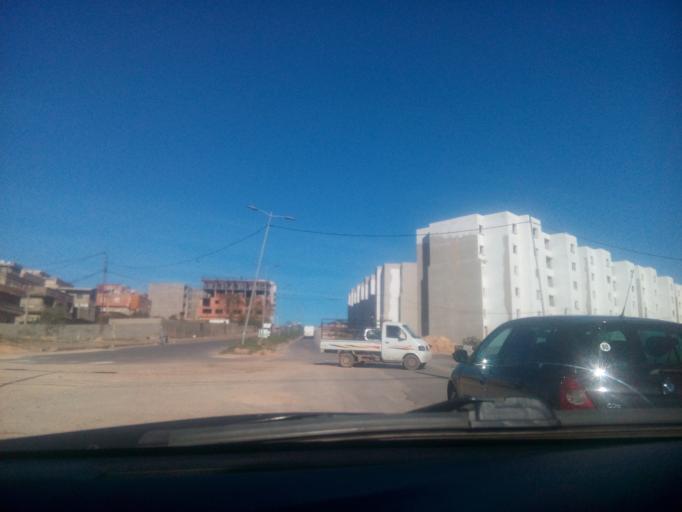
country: DZ
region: Oran
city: Bir el Djir
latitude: 35.7434
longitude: -0.5488
